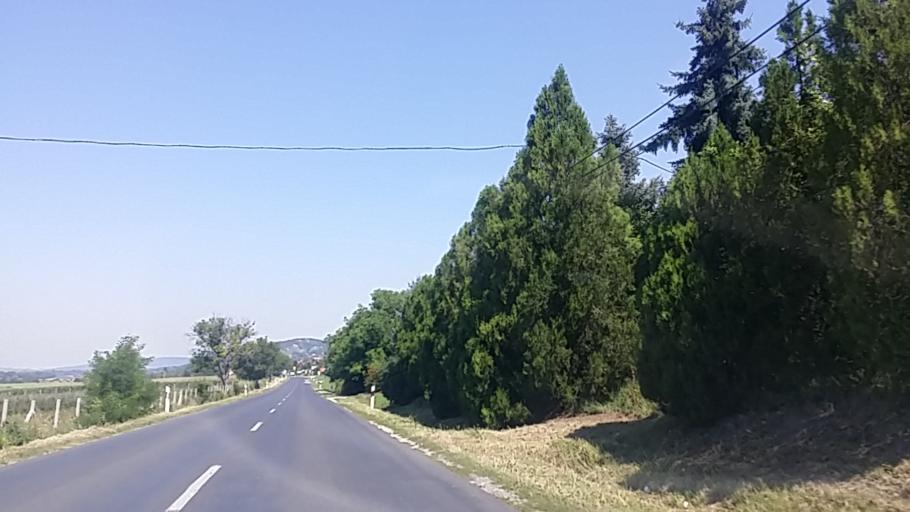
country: HU
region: Zala
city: Cserszegtomaj
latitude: 46.8004
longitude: 17.2067
